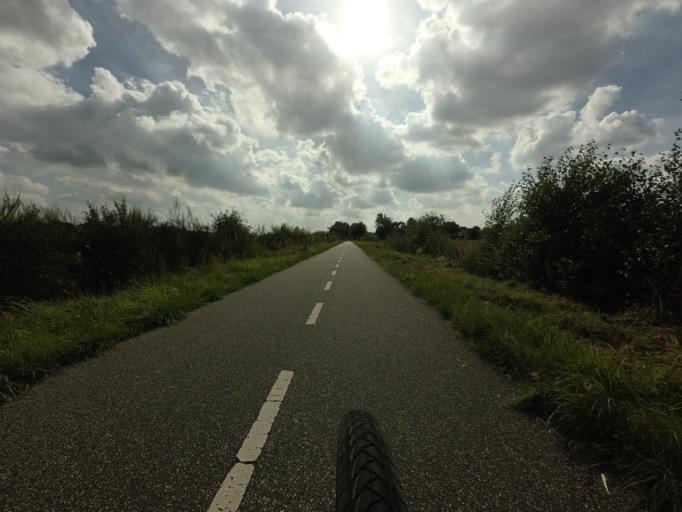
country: DK
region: Central Jutland
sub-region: Herning Kommune
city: Sunds
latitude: 56.1832
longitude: 9.0072
